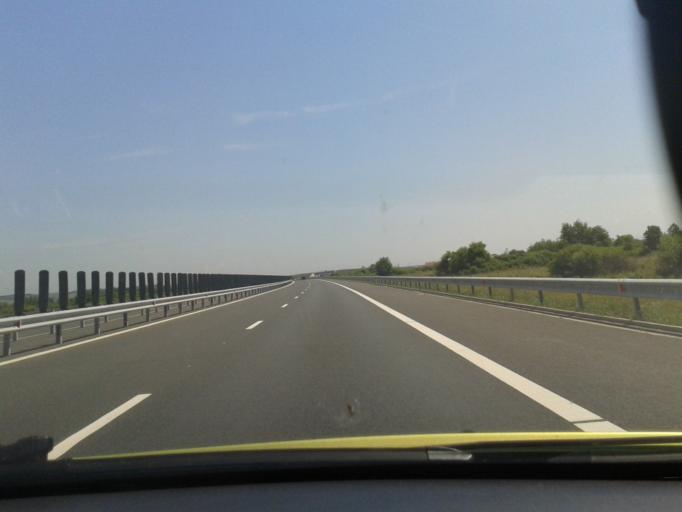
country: RO
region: Timis
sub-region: Comuna Bethausen
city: Bethausen
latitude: 45.8111
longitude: 21.9442
